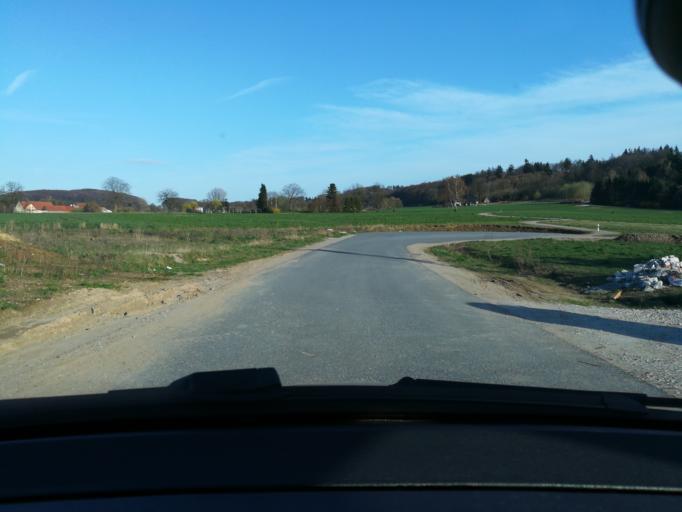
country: DE
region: North Rhine-Westphalia
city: Borgholzhausen
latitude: 52.0938
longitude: 8.2918
